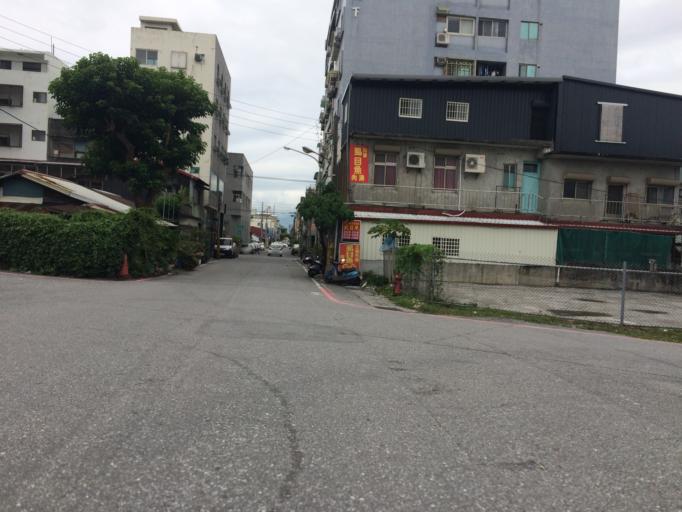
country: TW
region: Taiwan
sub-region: Hualien
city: Hualian
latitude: 23.9747
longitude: 121.6094
